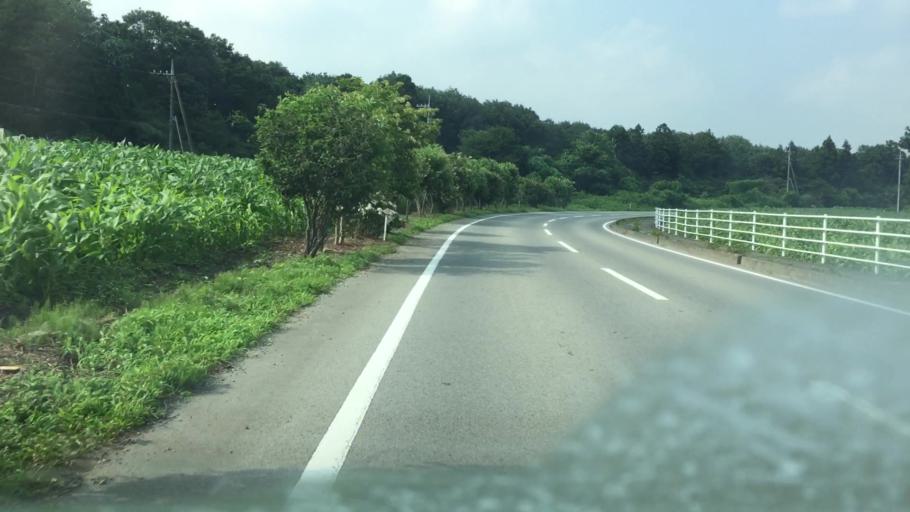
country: JP
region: Tochigi
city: Kuroiso
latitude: 36.9977
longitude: 139.9957
